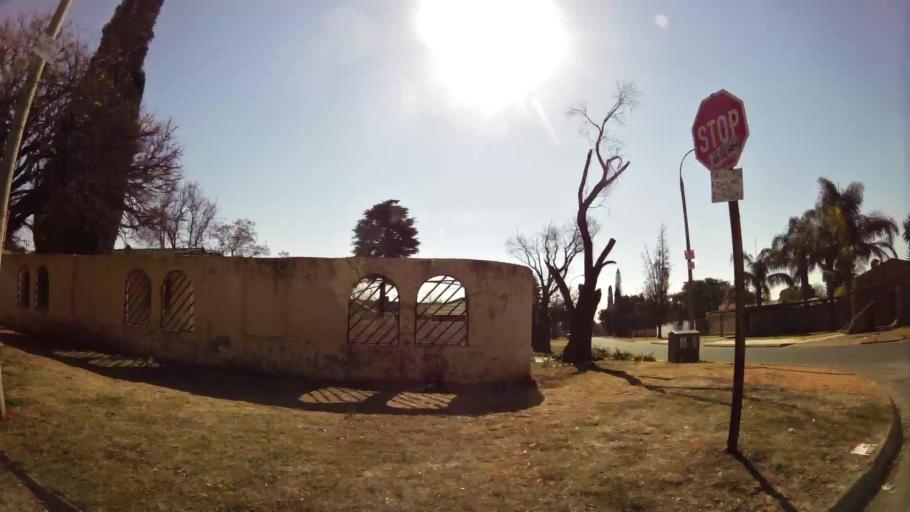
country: ZA
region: Gauteng
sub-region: Ekurhuleni Metropolitan Municipality
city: Tembisa
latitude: -26.0467
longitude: 28.2069
